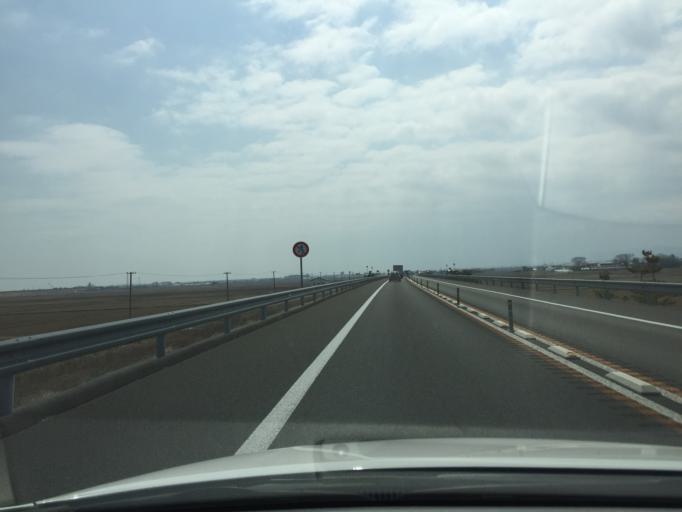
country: JP
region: Miyagi
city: Iwanuma
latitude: 38.0670
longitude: 140.8930
